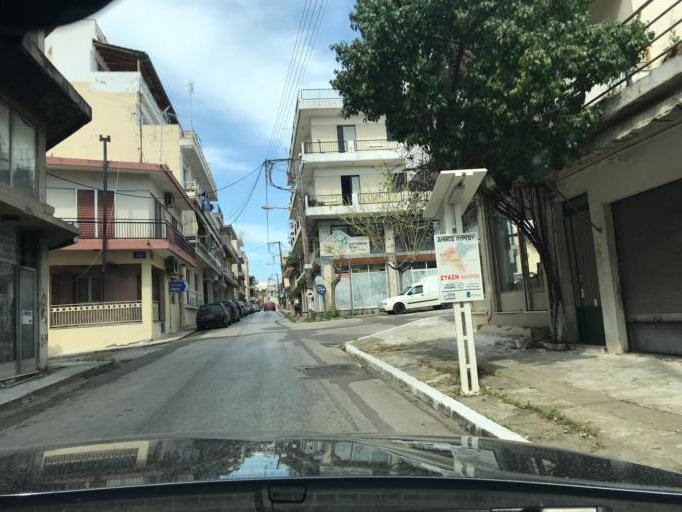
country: GR
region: West Greece
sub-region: Nomos Ileias
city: Pyrgos
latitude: 37.6722
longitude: 21.4468
